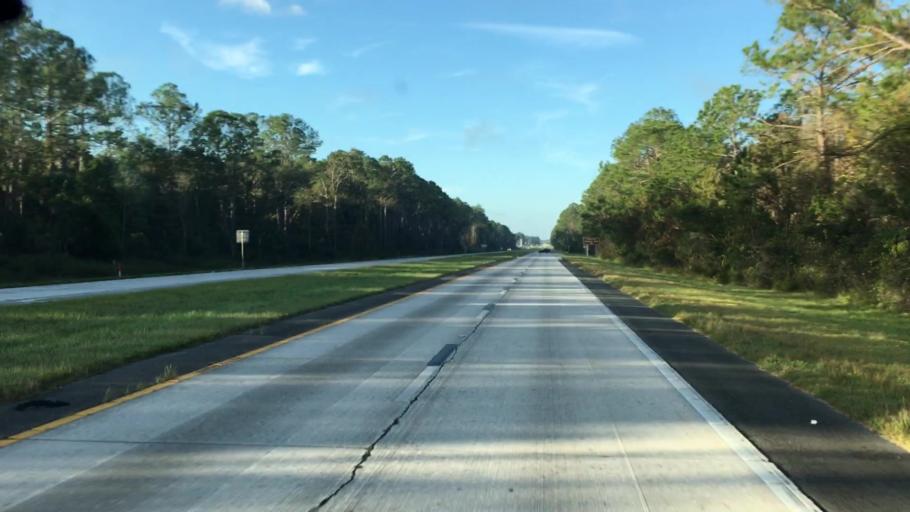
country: US
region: Florida
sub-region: Volusia County
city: North DeLand
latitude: 29.0781
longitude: -81.2445
